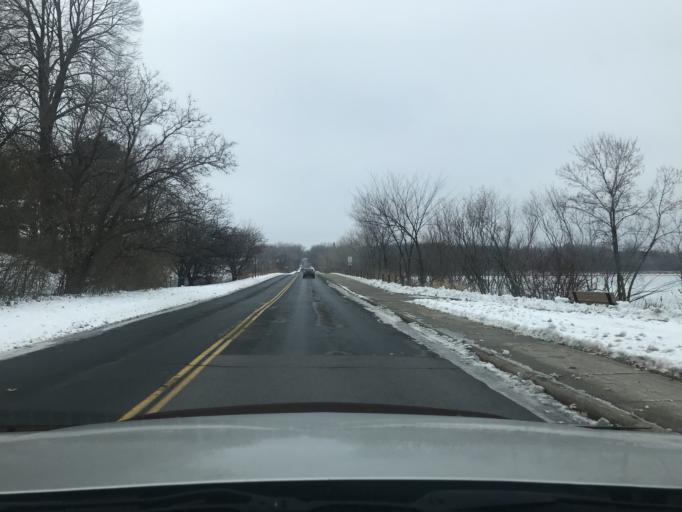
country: US
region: Minnesota
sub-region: Hennepin County
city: Edina
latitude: 44.8836
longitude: -93.3373
